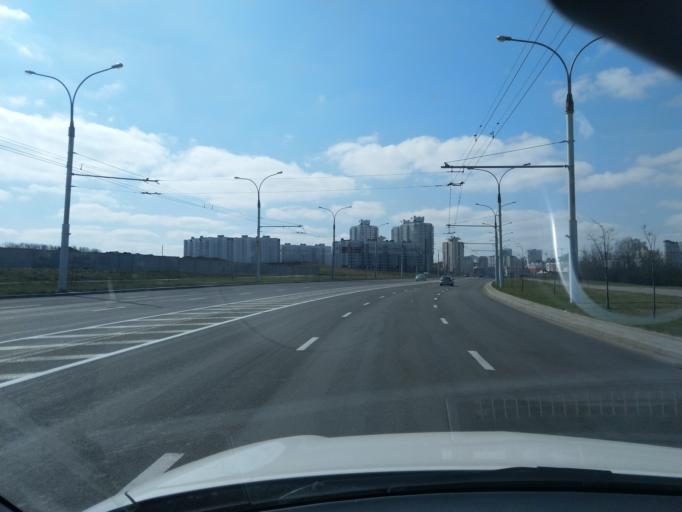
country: BY
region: Minsk
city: Yubilyeyny
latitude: 53.8556
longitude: 27.4970
